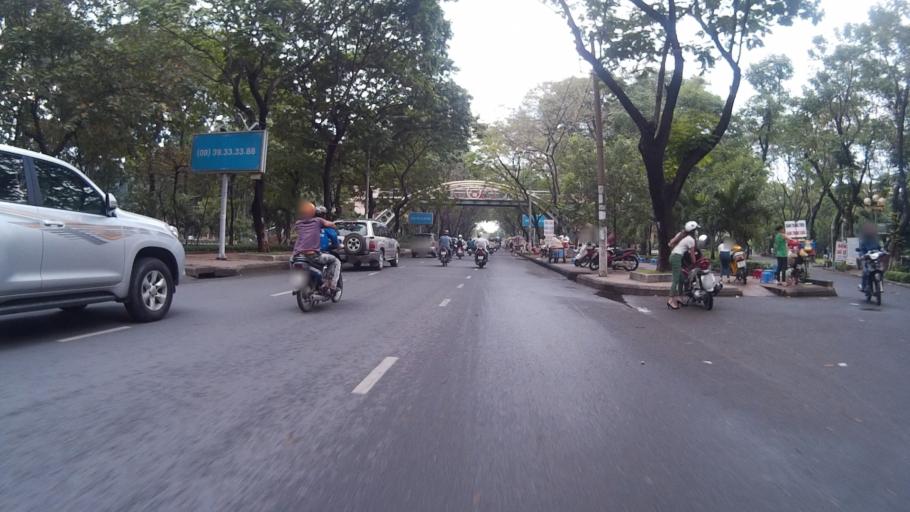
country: VN
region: Ho Chi Minh City
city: Quan Phu Nhuan
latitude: 10.8017
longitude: 106.6652
